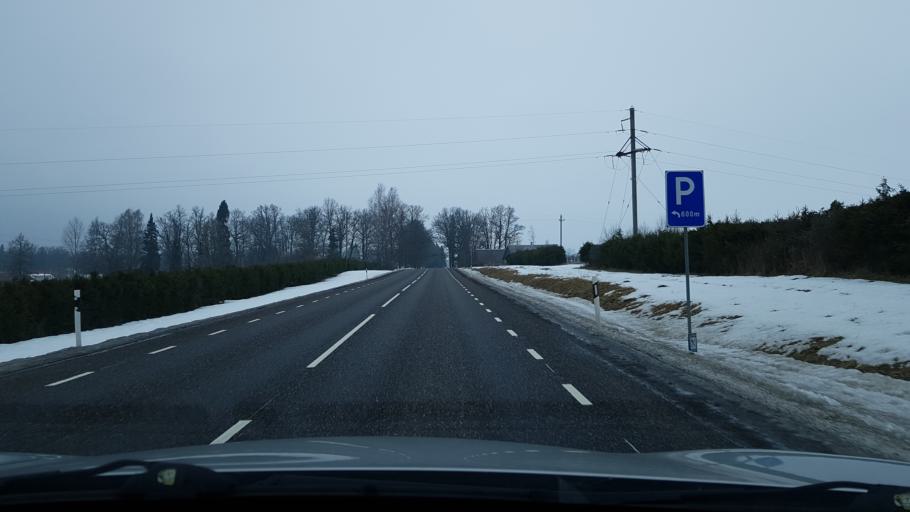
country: EE
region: Vorumaa
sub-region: Antsla vald
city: Vana-Antsla
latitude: 57.8988
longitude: 26.2889
